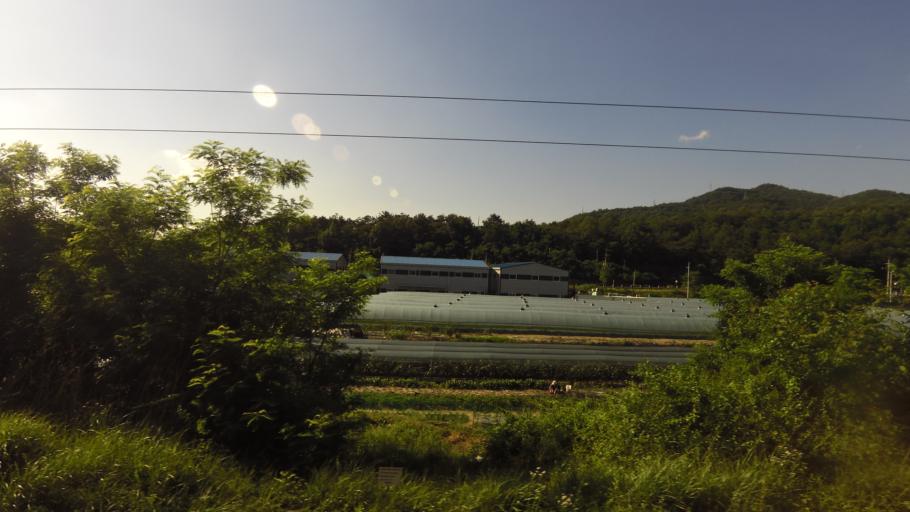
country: KR
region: Gyeongsangbuk-do
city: Waegwan
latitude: 35.9632
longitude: 128.4553
